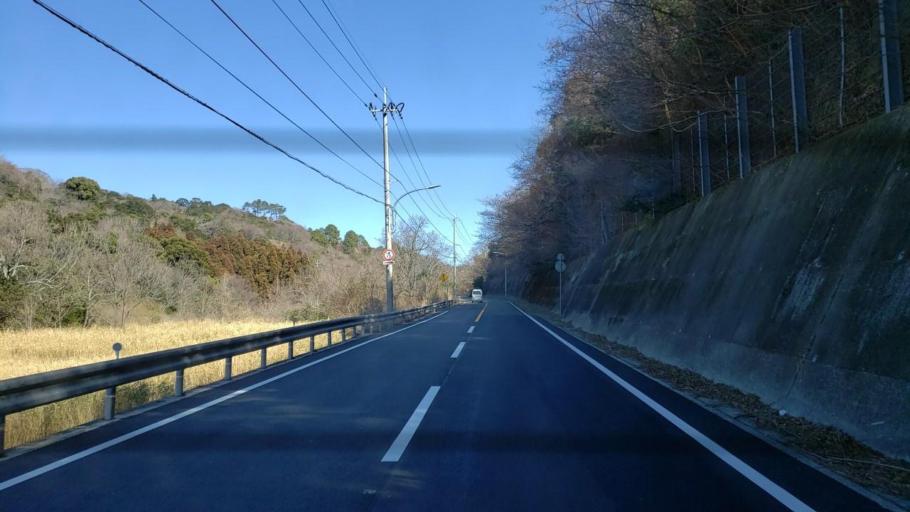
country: JP
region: Tokushima
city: Narutocho-mitsuishi
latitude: 34.2285
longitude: 134.5749
